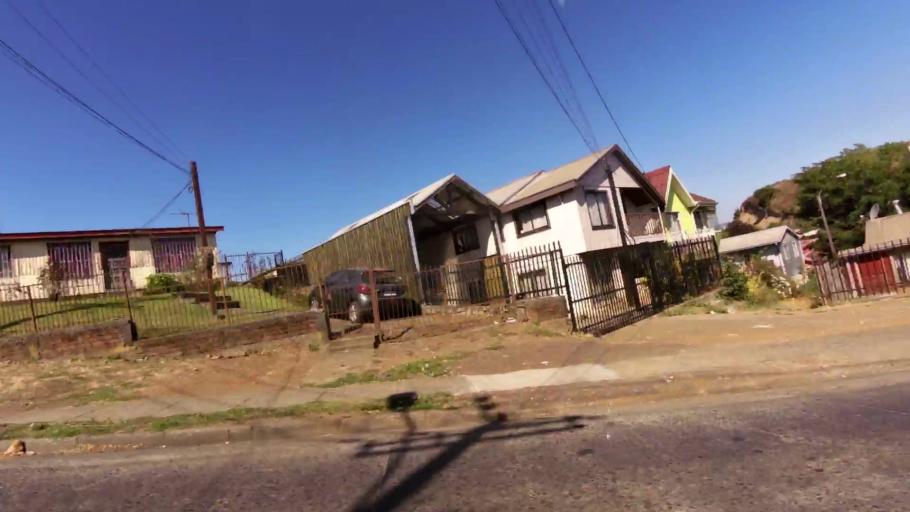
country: CL
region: Biobio
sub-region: Provincia de Concepcion
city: Concepcion
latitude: -36.7976
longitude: -73.0489
